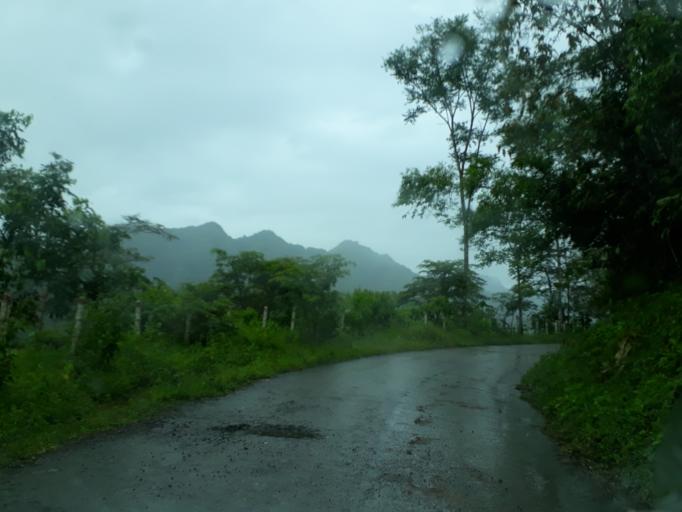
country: CO
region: Boyaca
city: Santa Maria
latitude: 4.7092
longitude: -73.2996
